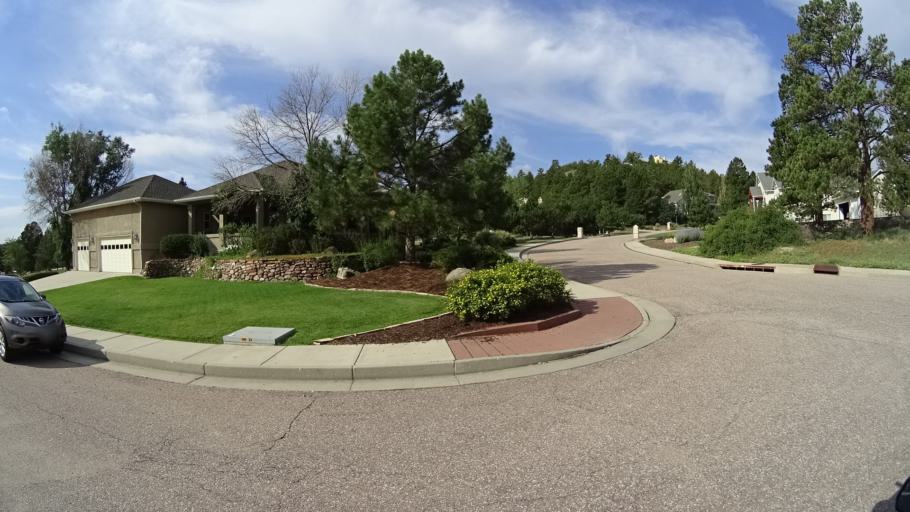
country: US
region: Colorado
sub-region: El Paso County
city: Air Force Academy
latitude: 38.9414
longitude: -104.8240
